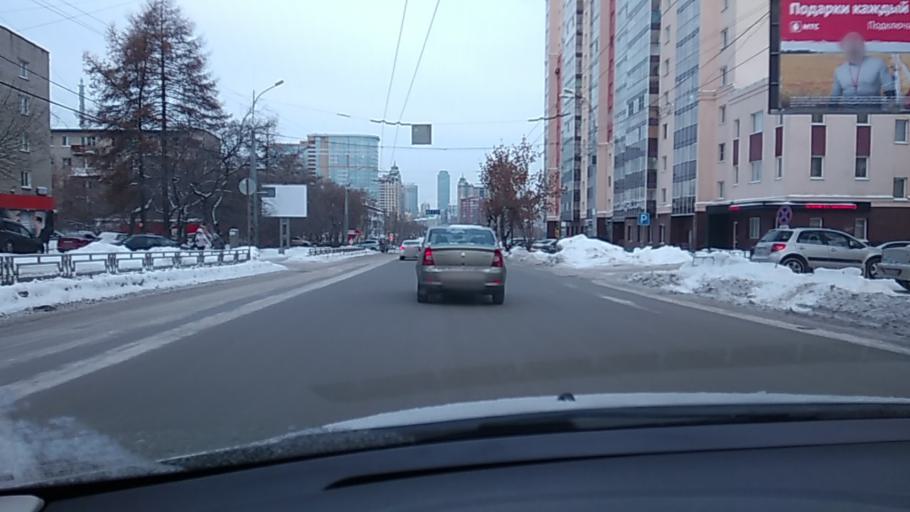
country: RU
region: Sverdlovsk
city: Yekaterinburg
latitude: 56.8152
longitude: 60.6211
